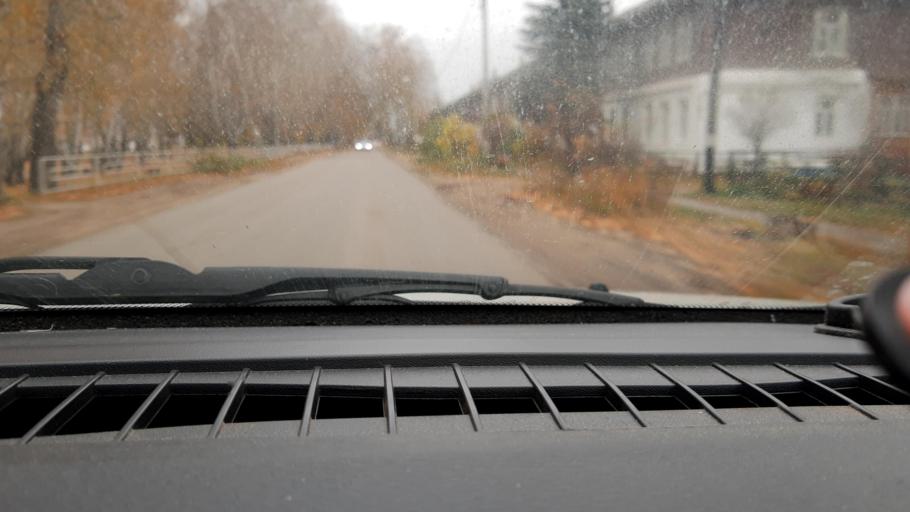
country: RU
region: Nizjnij Novgorod
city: Neklyudovo
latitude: 56.4089
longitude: 44.0289
